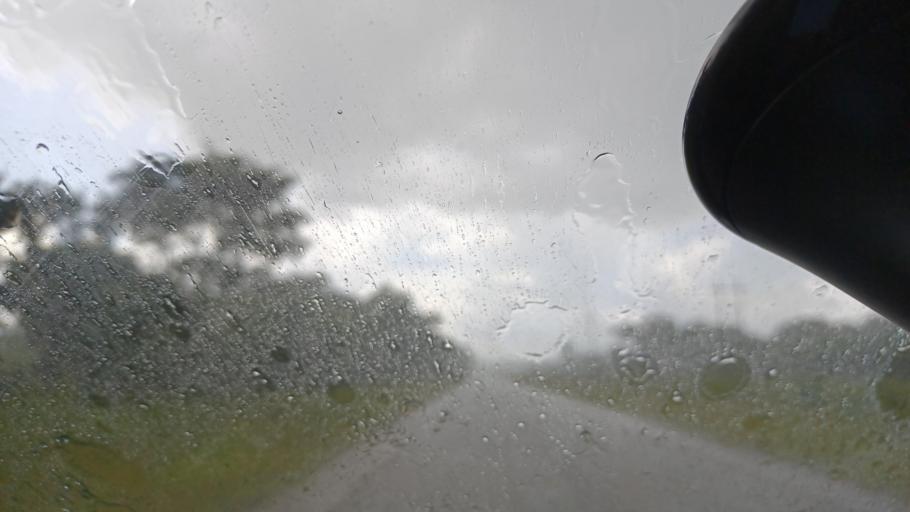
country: ZM
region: North-Western
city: Kasempa
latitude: -13.0973
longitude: 25.9068
